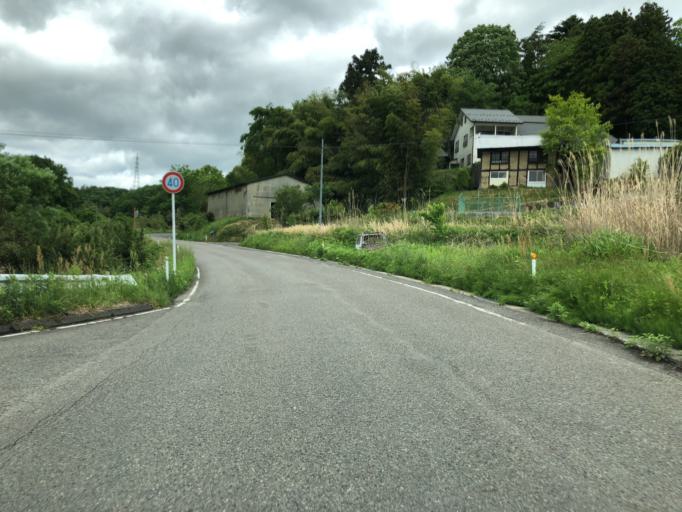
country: JP
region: Fukushima
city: Miharu
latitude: 37.4611
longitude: 140.4698
